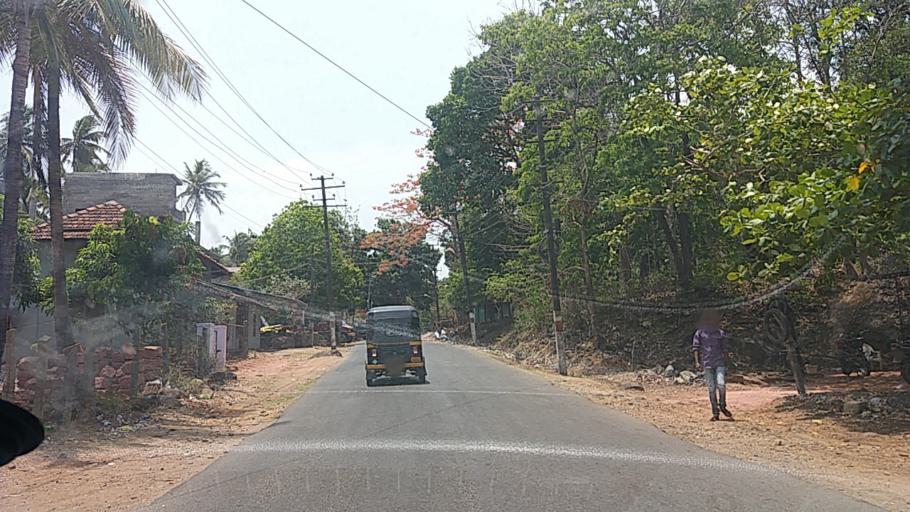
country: IN
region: Karnataka
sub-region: Uttar Kannada
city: Karwar
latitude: 14.8113
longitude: 74.1539
